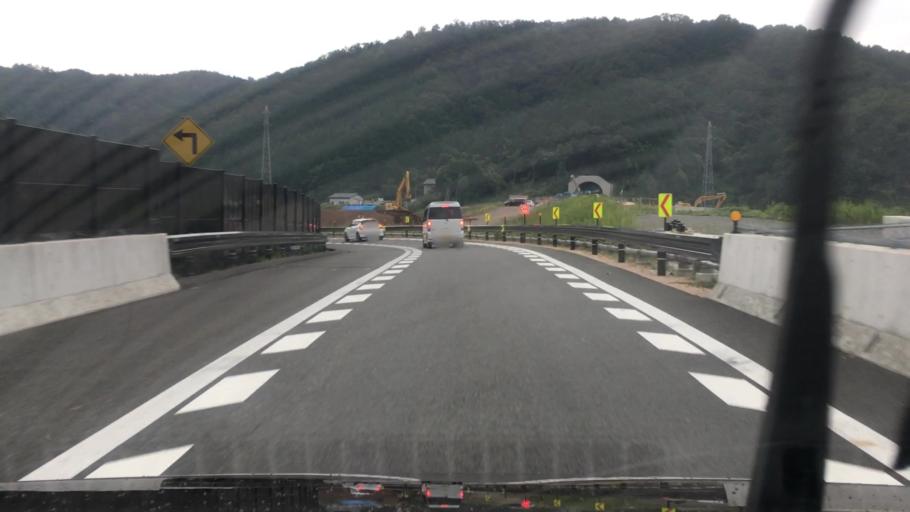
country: JP
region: Hyogo
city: Toyooka
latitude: 35.4659
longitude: 134.7633
